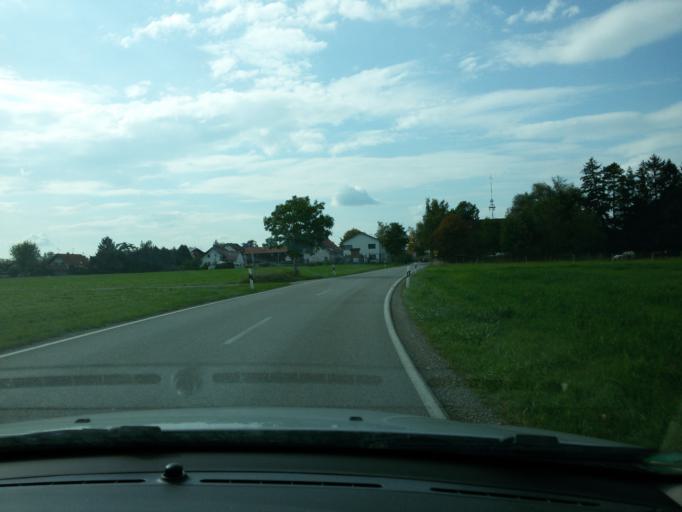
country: DE
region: Bavaria
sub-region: Swabia
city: Lamerdingen
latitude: 48.0928
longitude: 10.7442
